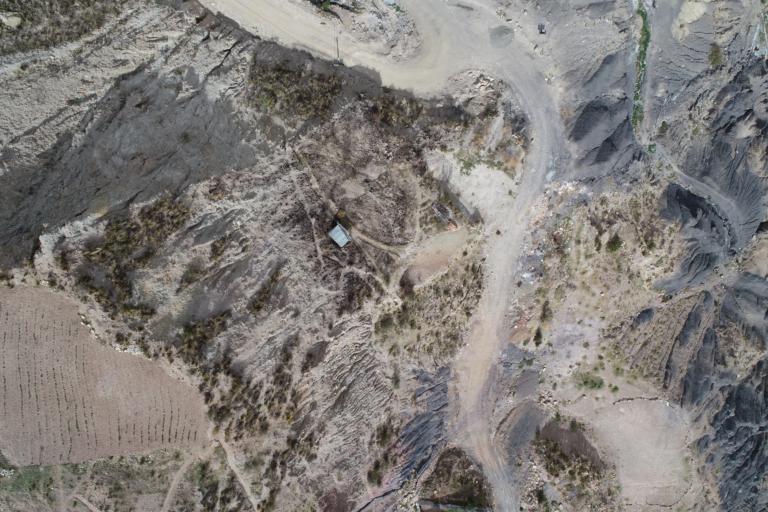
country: BO
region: La Paz
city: La Paz
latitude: -16.5529
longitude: -68.0548
